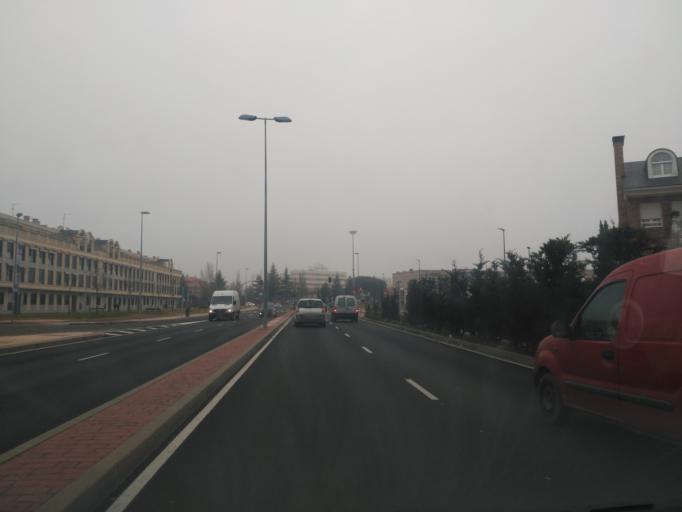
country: ES
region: Castille and Leon
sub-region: Provincia de Salamanca
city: Santa Marta de Tormes
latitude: 40.9524
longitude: -5.6412
